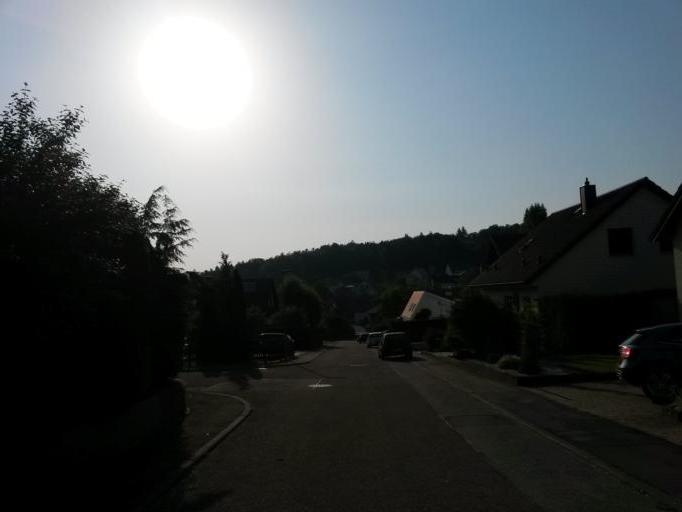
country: DE
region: Baden-Wuerttemberg
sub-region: Karlsruhe Region
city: Neuenburg
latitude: 48.8887
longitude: 8.5652
